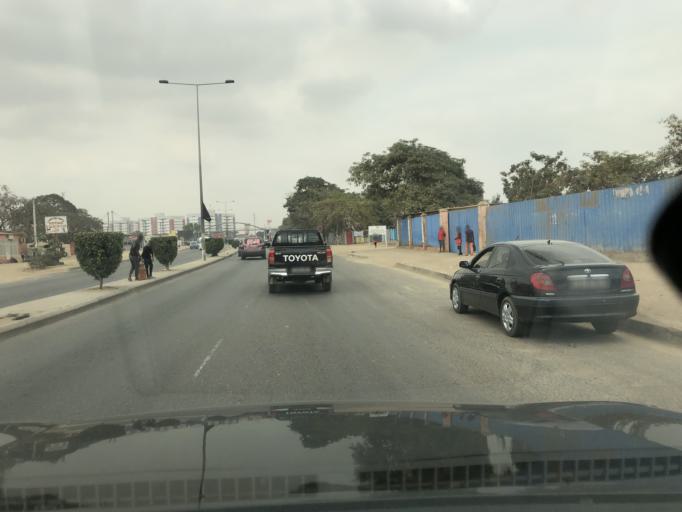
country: AO
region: Luanda
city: Luanda
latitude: -8.8428
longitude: 13.2841
